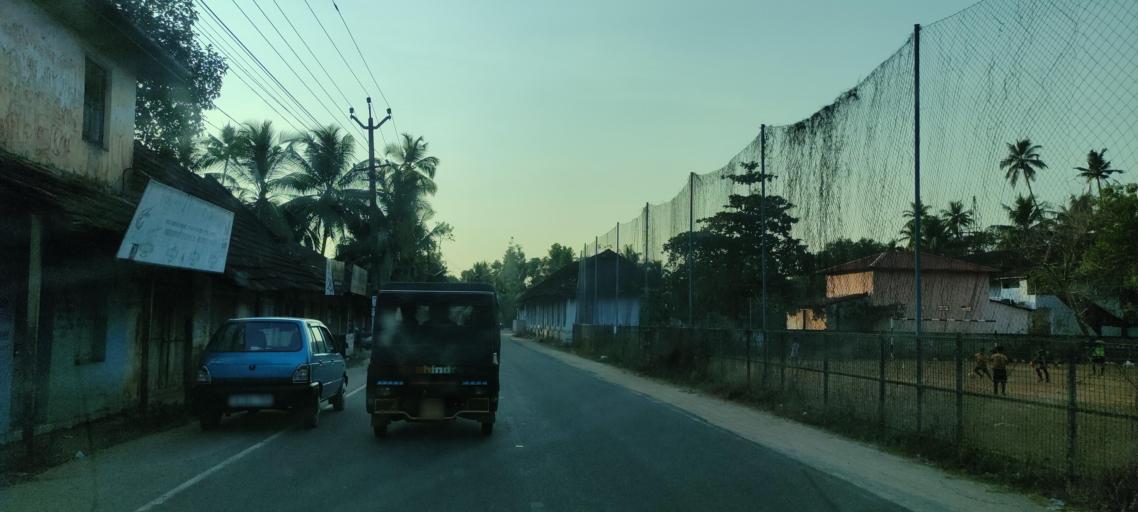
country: IN
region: Kerala
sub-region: Alappuzha
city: Kutiatodu
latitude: 9.7746
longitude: 76.3396
